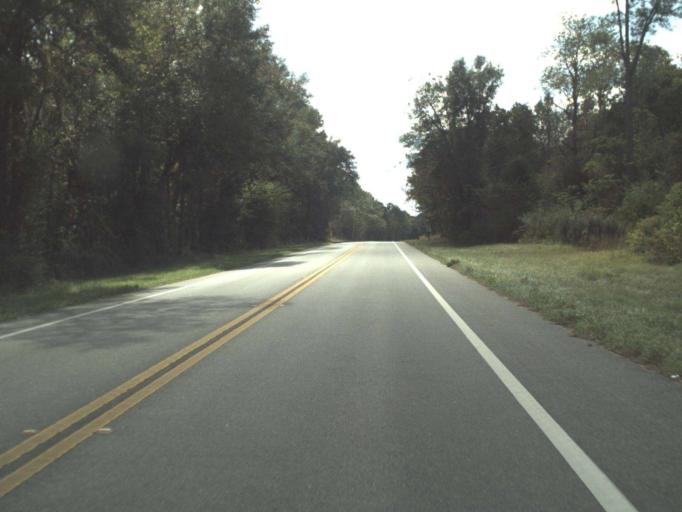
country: US
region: Florida
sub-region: Holmes County
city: Bonifay
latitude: 30.7180
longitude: -85.6163
